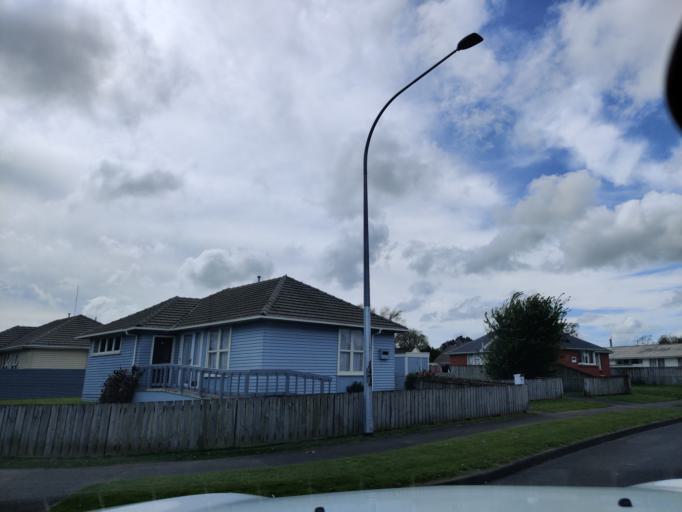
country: NZ
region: Manawatu-Wanganui
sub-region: Palmerston North City
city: Palmerston North
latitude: -40.3586
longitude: 175.5858
